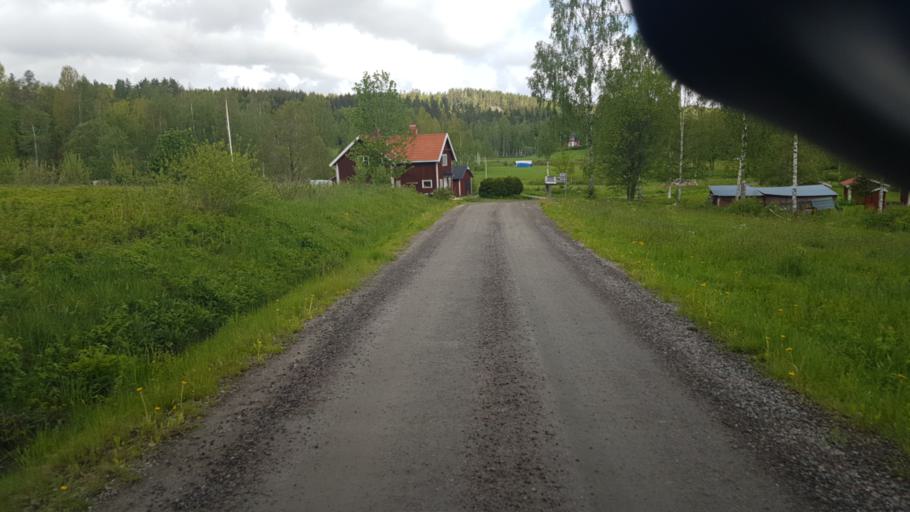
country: NO
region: Ostfold
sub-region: Romskog
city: Romskog
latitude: 59.8628
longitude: 11.9700
